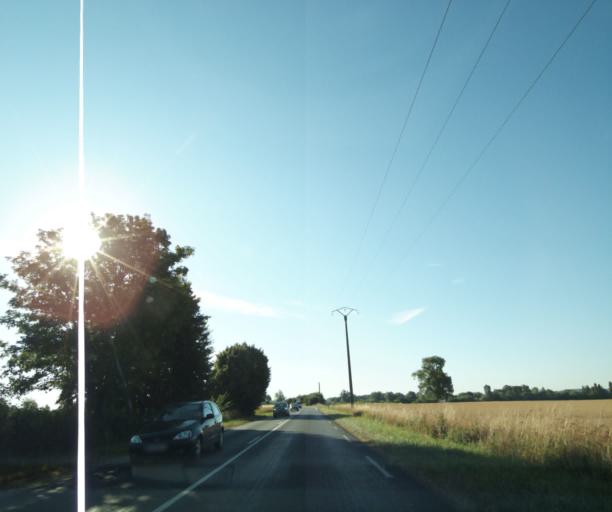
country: FR
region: Ile-de-France
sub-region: Departement de Seine-et-Marne
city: Cannes-Ecluse
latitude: 48.3797
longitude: 2.9824
